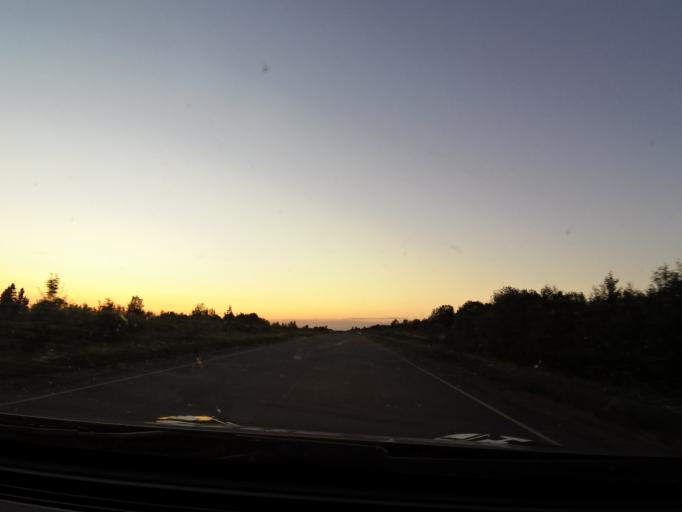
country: RU
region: Vologda
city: Vytegra
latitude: 60.9402
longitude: 36.0908
